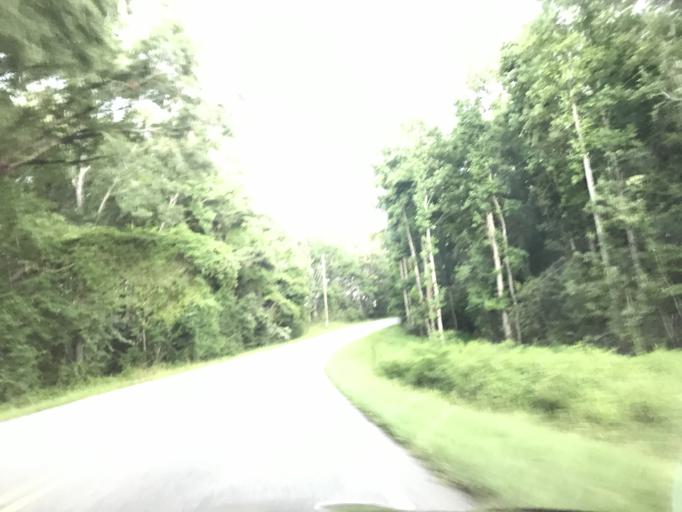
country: US
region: North Carolina
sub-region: Johnston County
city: Four Oaks
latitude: 35.5308
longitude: -78.4356
